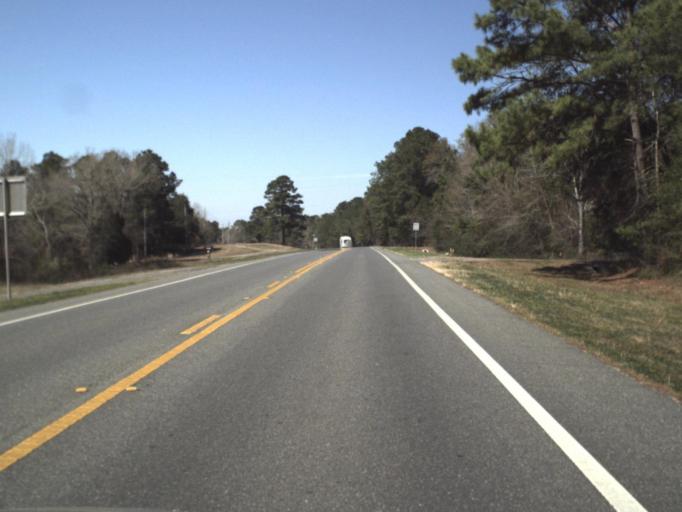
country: US
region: Florida
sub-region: Jackson County
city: Marianna
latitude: 30.7898
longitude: -85.3583
